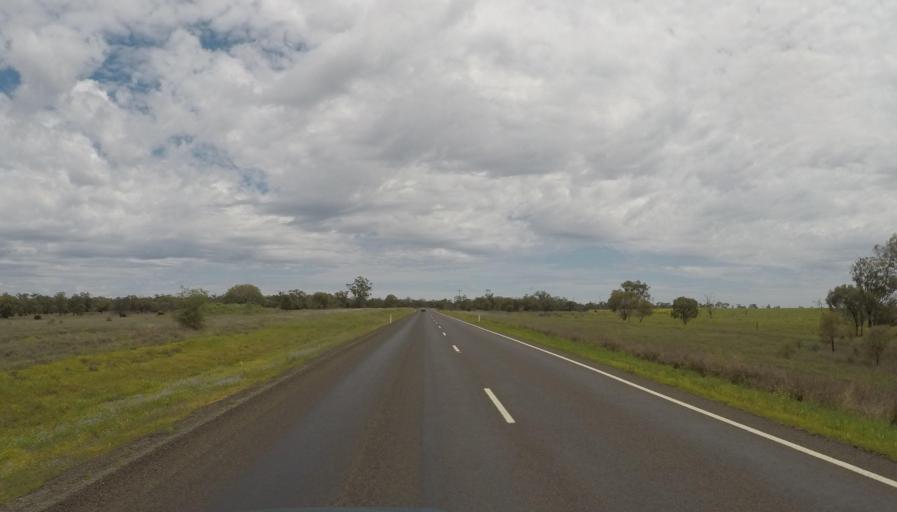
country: AU
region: Queensland
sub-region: Maranoa
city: Roma
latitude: -26.4897
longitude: 147.8789
